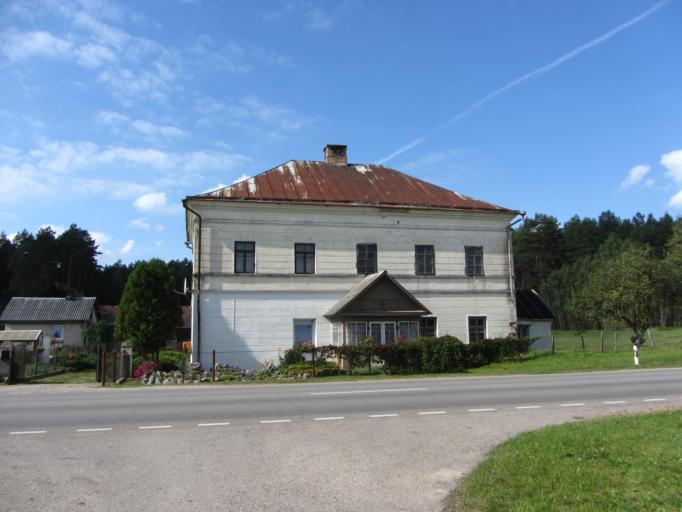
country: LT
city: Skaidiskes
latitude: 54.4741
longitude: 25.3188
